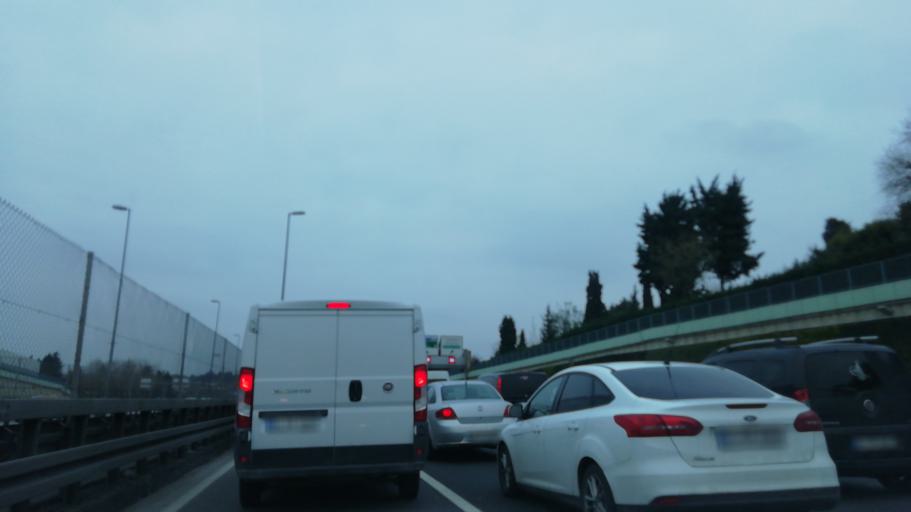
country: TR
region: Istanbul
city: Istanbul
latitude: 41.0251
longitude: 28.9224
